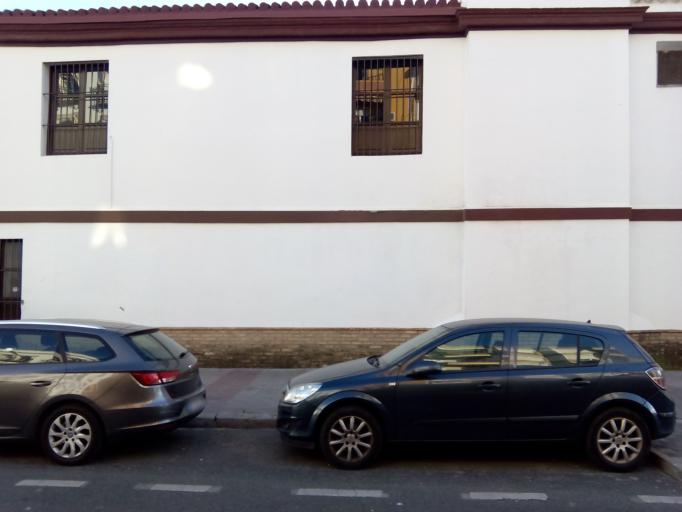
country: ES
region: Andalusia
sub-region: Provincia de Sevilla
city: Sevilla
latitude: 37.3825
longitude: -6.0021
